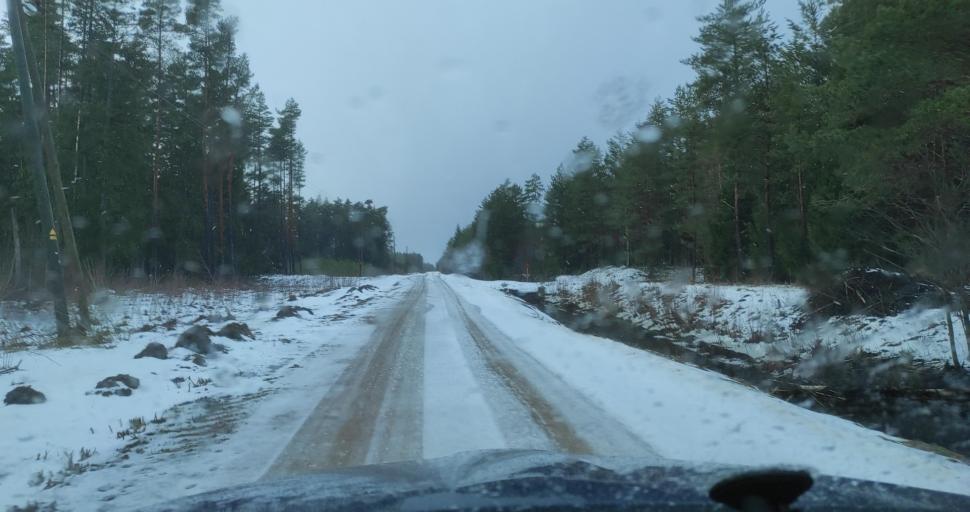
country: LV
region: Dundaga
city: Dundaga
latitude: 57.3801
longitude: 22.1580
